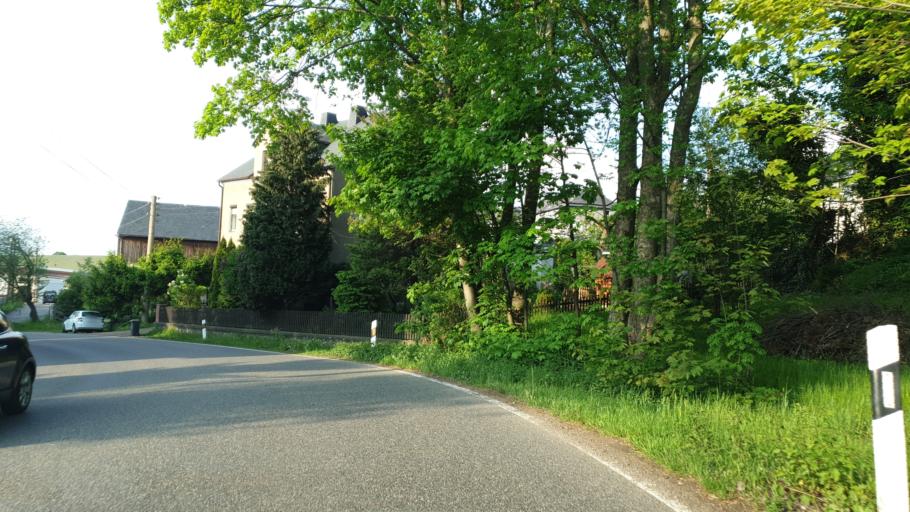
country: DE
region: Saxony
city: Stollberg
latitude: 50.7049
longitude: 12.7869
